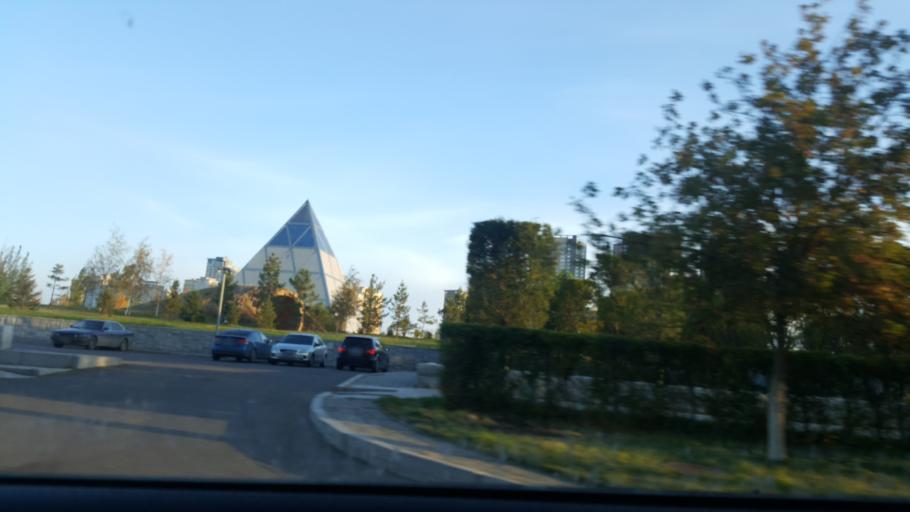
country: KZ
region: Astana Qalasy
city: Astana
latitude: 51.1209
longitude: 71.4664
